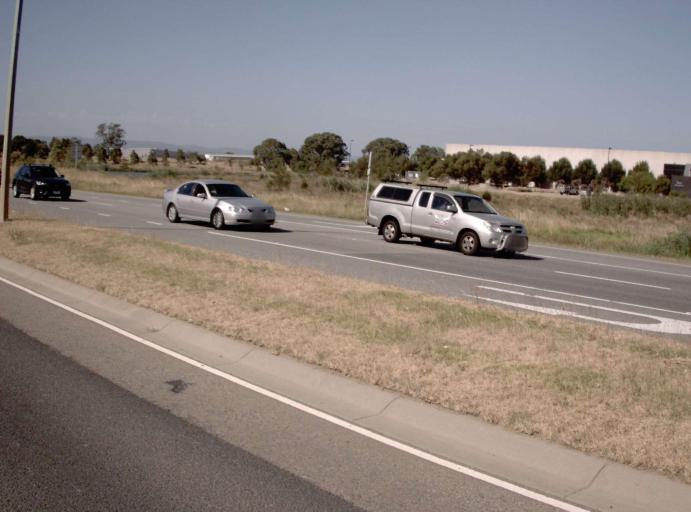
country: AU
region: Victoria
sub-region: Frankston
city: Sandhurst
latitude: -38.0476
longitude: 145.2087
